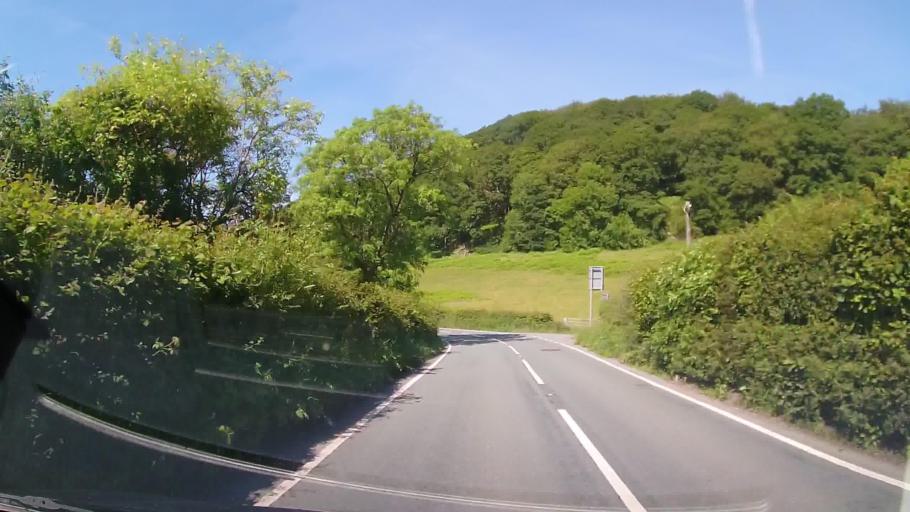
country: GB
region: Wales
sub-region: Sir Powys
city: Machynlleth
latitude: 52.5984
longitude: -3.8636
